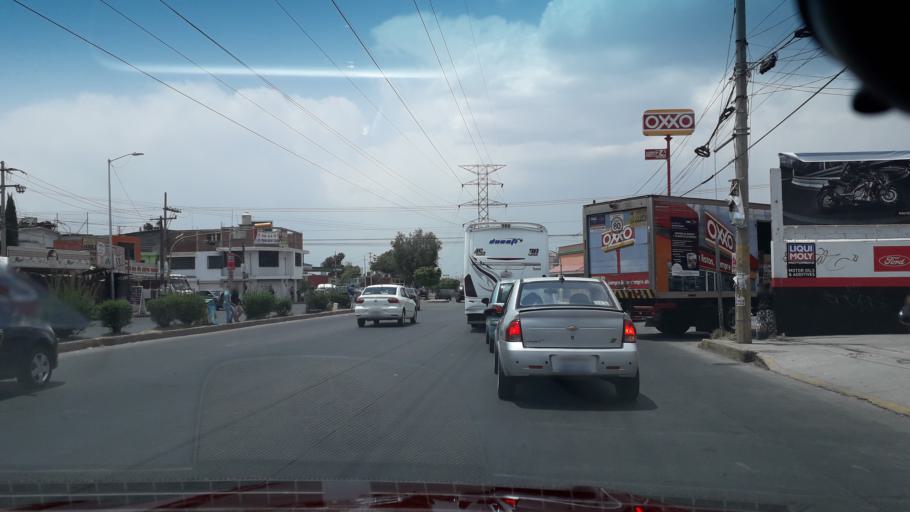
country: MX
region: Puebla
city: Puebla
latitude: 19.0036
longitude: -98.2342
